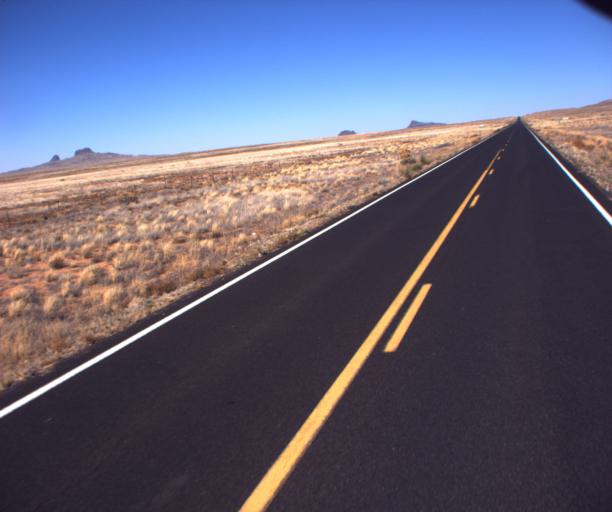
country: US
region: Arizona
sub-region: Navajo County
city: Dilkon
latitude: 35.3723
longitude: -110.4251
